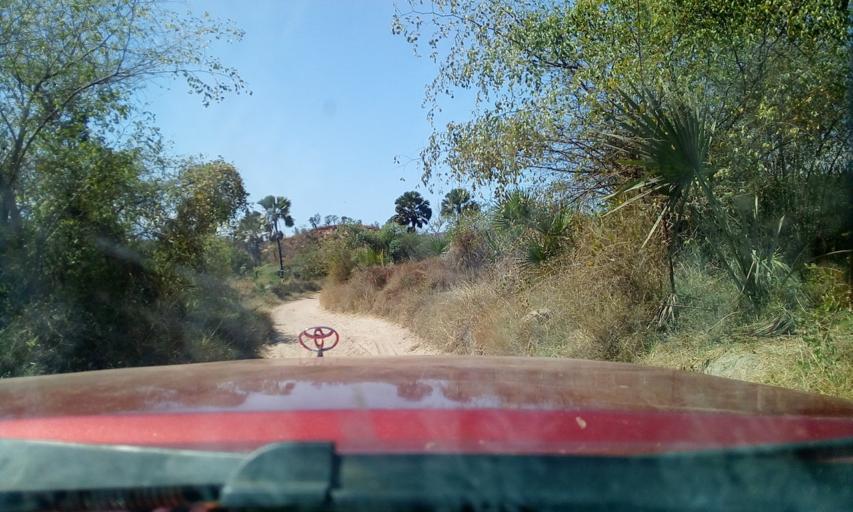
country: MG
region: Boeny
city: Sitampiky
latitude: -16.1270
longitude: 45.4839
